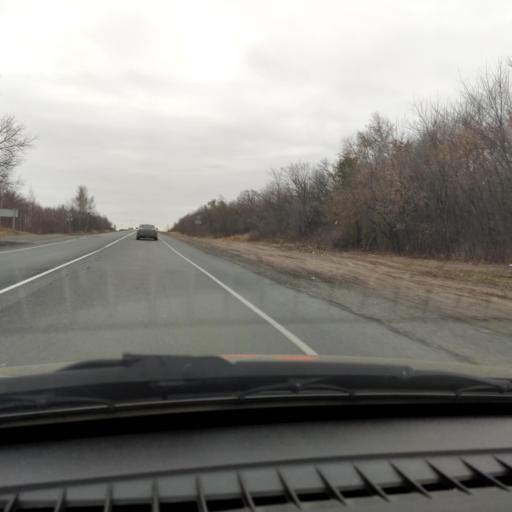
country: RU
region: Samara
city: Zhigulevsk
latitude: 53.3525
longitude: 49.4536
